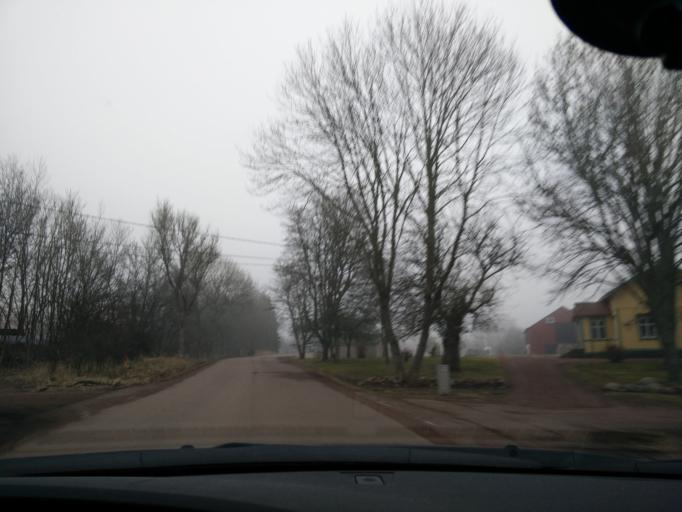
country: AX
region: Mariehamns stad
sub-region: Mariehamn
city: Mariehamn
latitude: 60.1050
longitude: 19.9000
